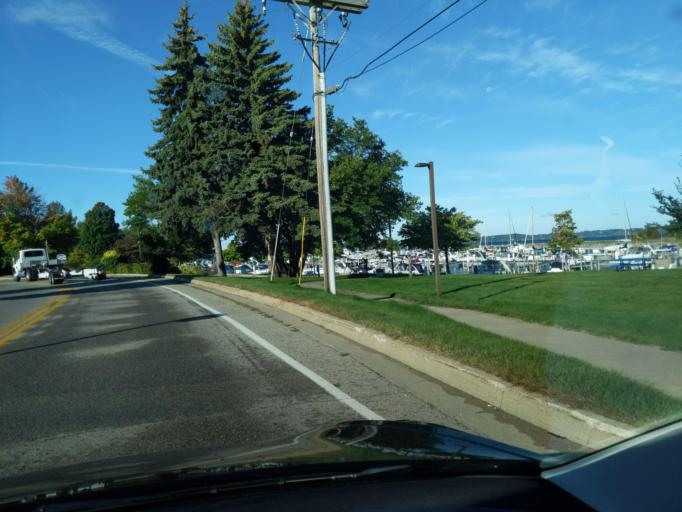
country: US
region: Michigan
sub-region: Antrim County
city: Elk Rapids
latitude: 44.9006
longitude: -85.4127
